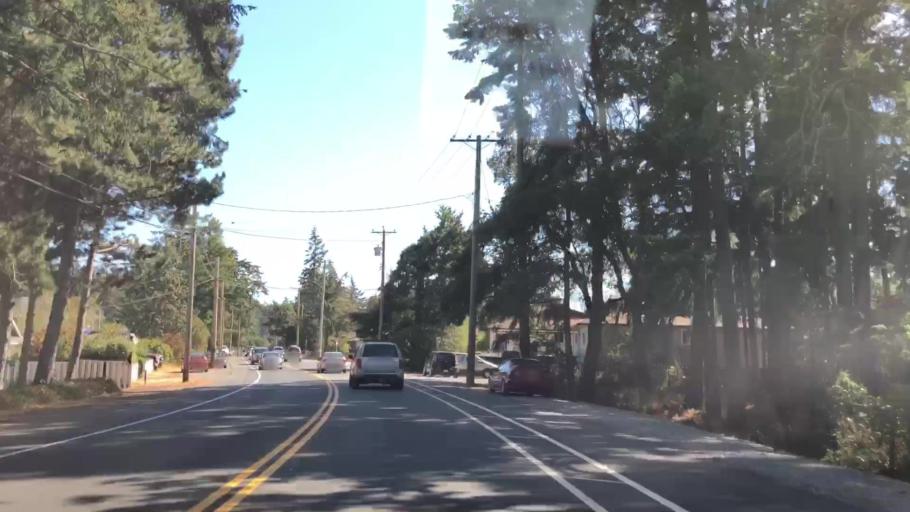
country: CA
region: British Columbia
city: Colwood
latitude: 48.4289
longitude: -123.4936
